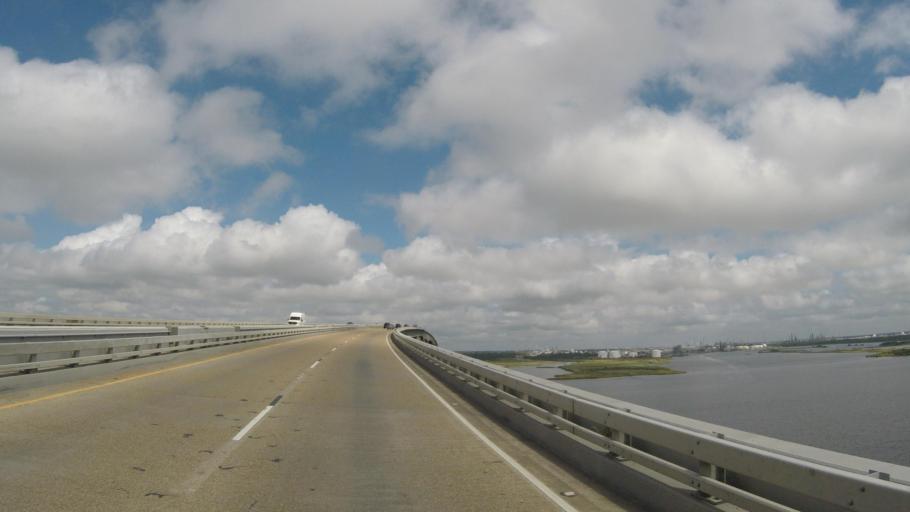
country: US
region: Louisiana
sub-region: Calcasieu Parish
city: Prien
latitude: 30.1986
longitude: -93.2777
